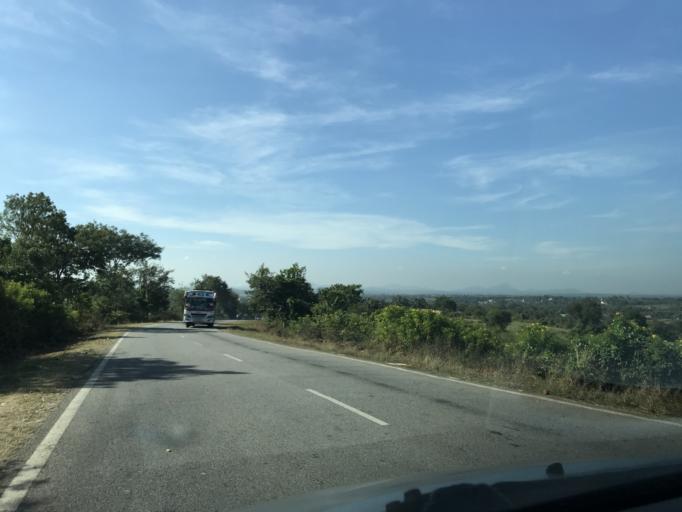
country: IN
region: Karnataka
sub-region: Mysore
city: Nanjangud
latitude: 12.1368
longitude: 76.5087
